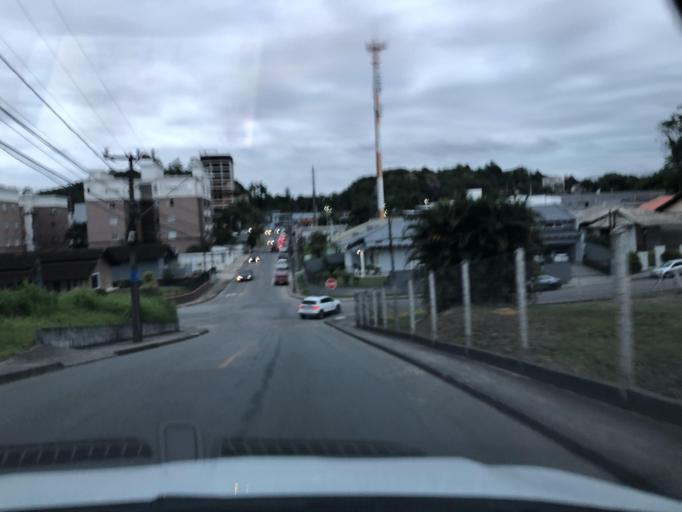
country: BR
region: Santa Catarina
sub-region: Joinville
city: Joinville
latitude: -26.2906
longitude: -48.8778
